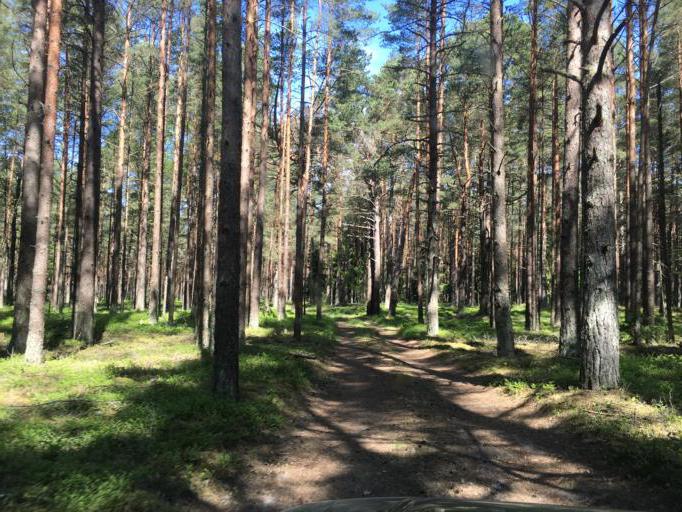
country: LV
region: Ventspils
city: Ventspils
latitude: 57.4711
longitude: 21.6486
